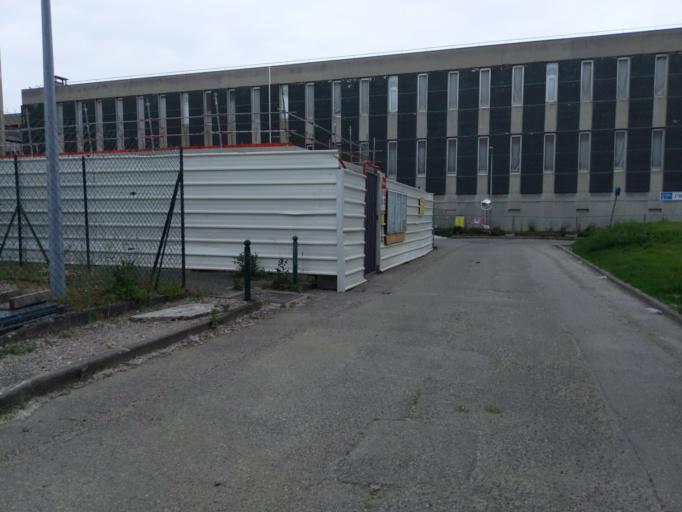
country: FR
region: Rhone-Alpes
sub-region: Departement du Rhone
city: Villeurbanne
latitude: 45.7806
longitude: 4.8693
